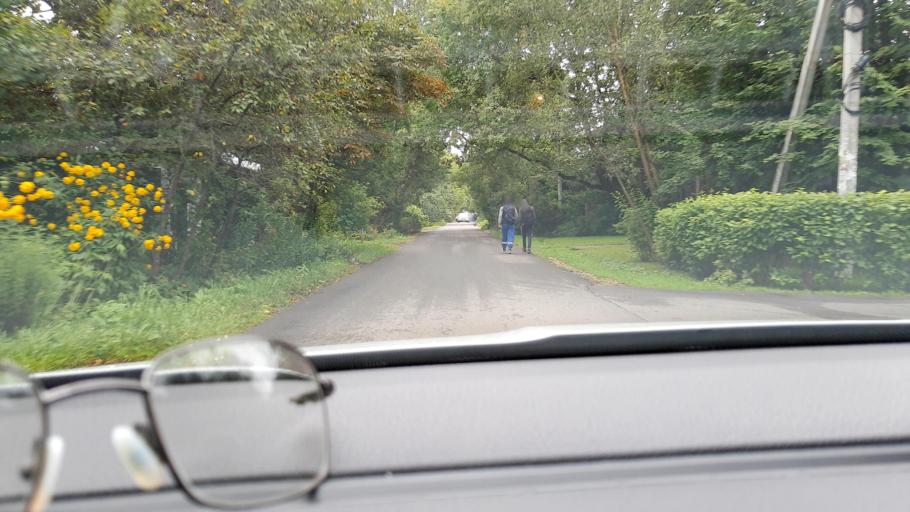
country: RU
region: Moskovskaya
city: Kokoshkino
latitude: 55.5948
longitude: 37.1727
